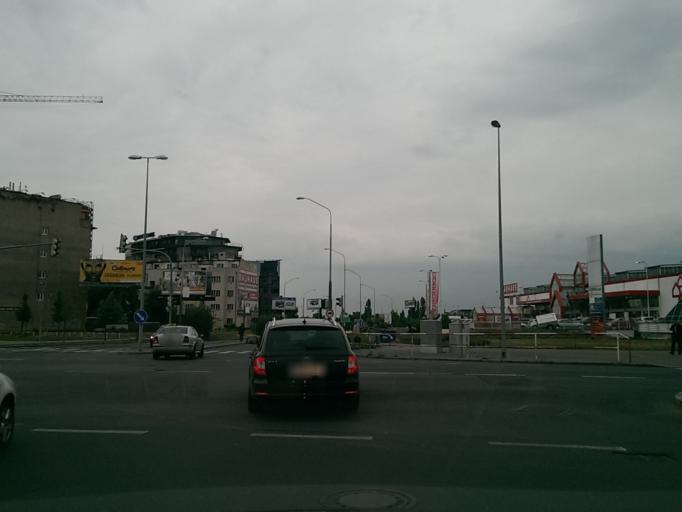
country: CZ
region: Praha
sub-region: Praha 2
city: Vysehrad
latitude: 50.0499
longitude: 14.4411
